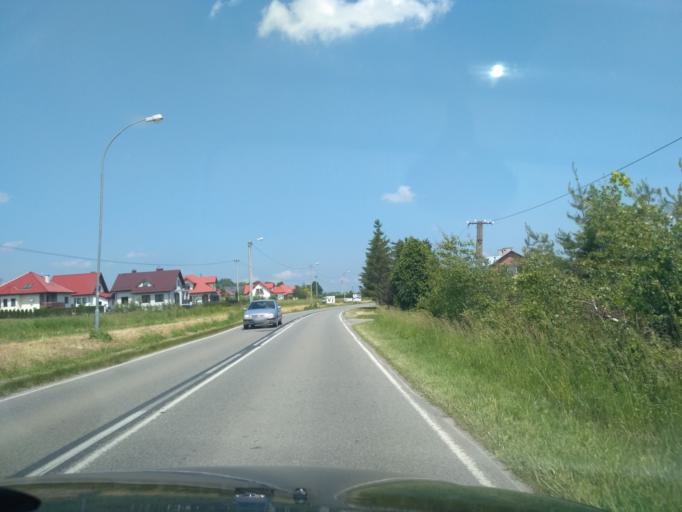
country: PL
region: Subcarpathian Voivodeship
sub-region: Powiat lancucki
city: Albigowa
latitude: 50.0234
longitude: 22.2243
